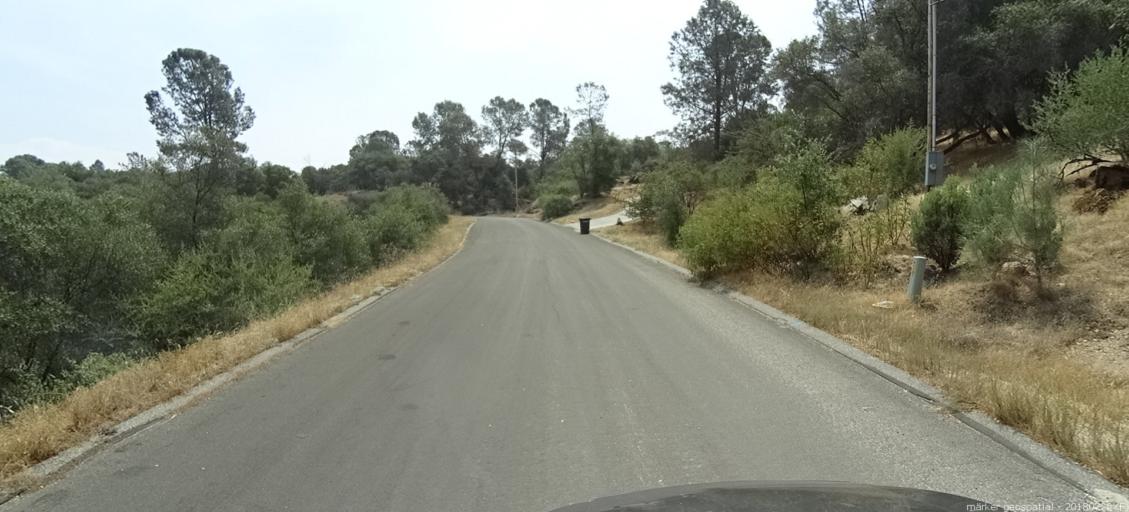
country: US
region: California
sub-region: Madera County
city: Coarsegold
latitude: 37.2446
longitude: -119.6949
